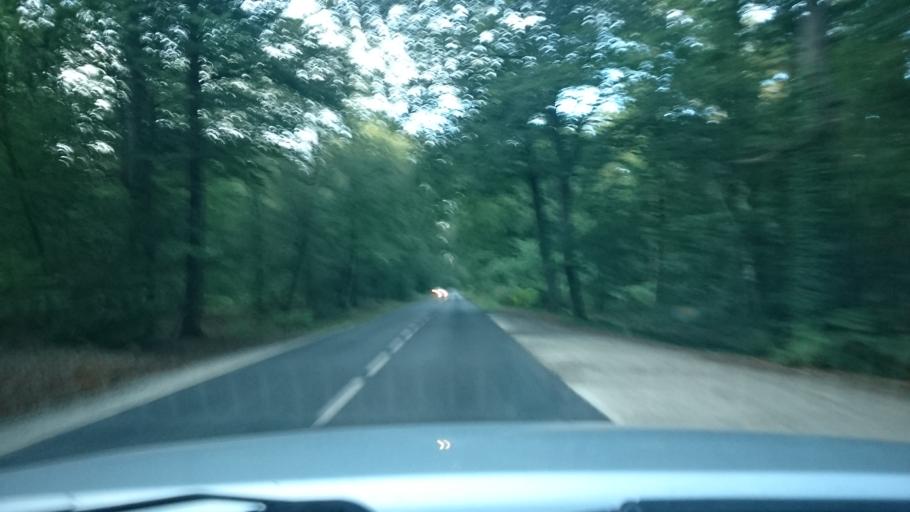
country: FR
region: Ile-de-France
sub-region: Departement de Seine-et-Marne
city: Bois-le-Roi
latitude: 48.4453
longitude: 2.7191
